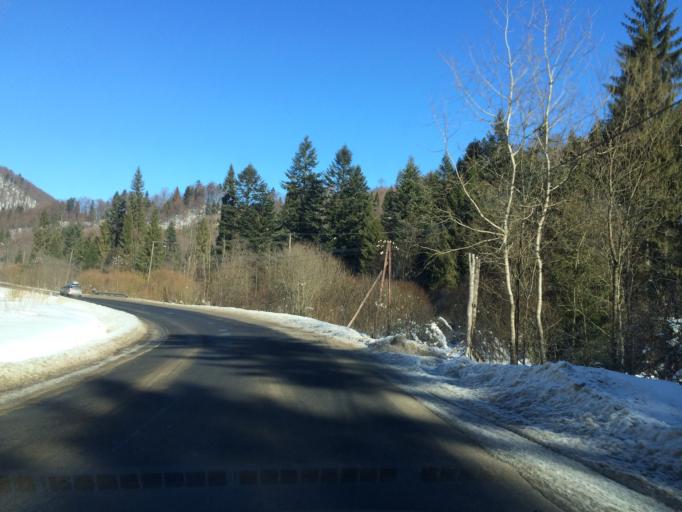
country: PL
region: Subcarpathian Voivodeship
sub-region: Powiat leski
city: Cisna
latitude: 49.2178
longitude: 22.3649
